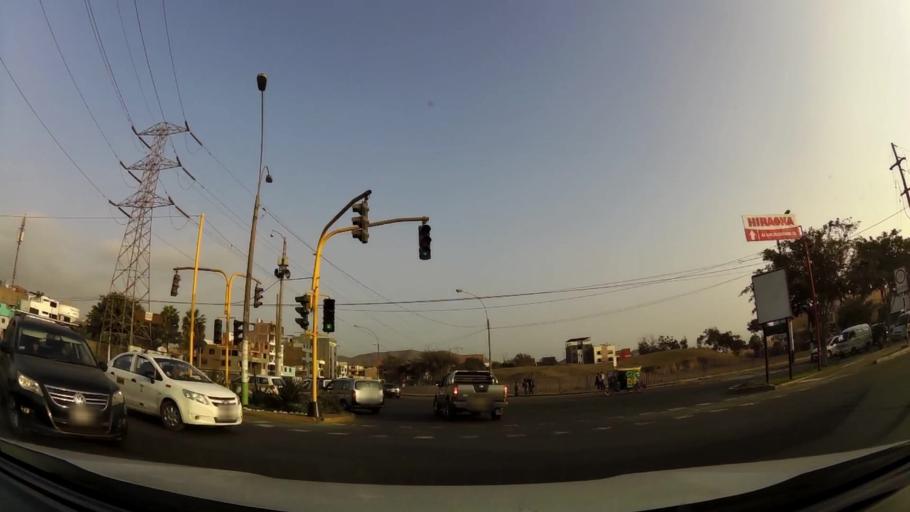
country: PE
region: Lima
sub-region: Lima
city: Independencia
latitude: -11.9837
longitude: -77.0723
